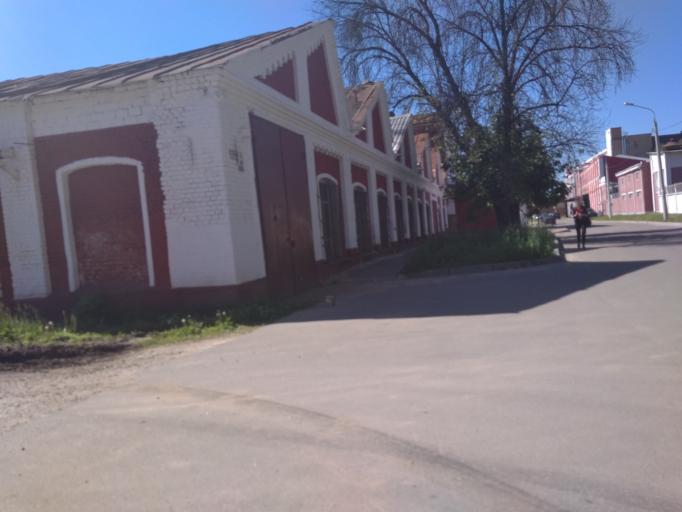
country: RU
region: Moskovskaya
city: Orekhovo-Zuyevo
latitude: 55.8047
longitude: 38.9910
